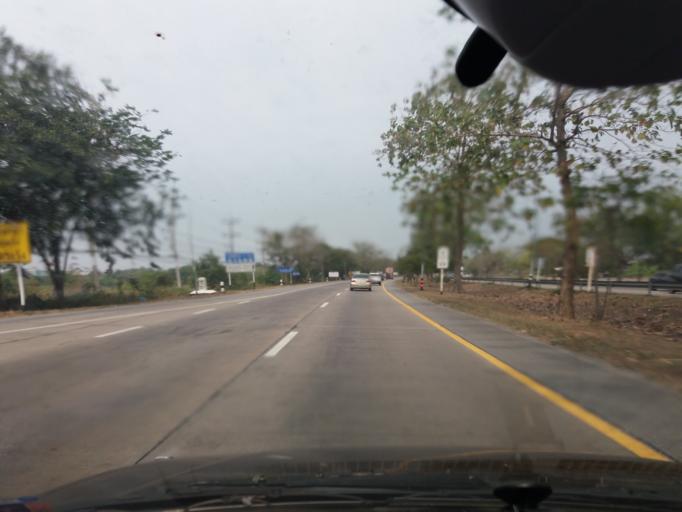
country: TH
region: Suphan Buri
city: Ban Sam Chuk
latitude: 14.7084
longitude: 100.1022
